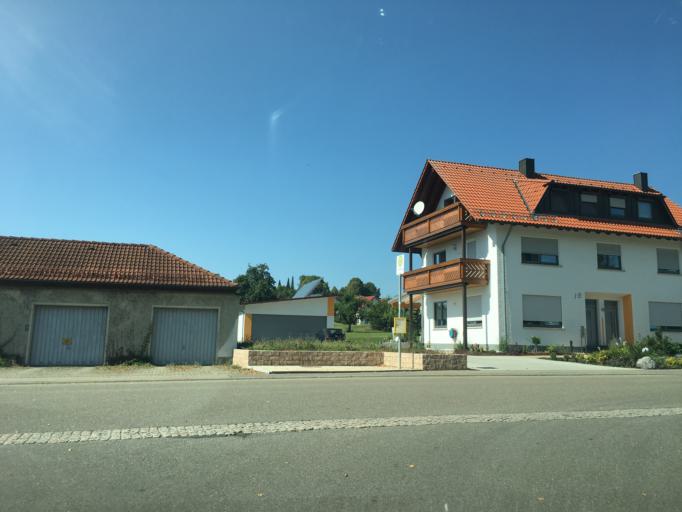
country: DE
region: Baden-Wuerttemberg
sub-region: Tuebingen Region
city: Hayingen
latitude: 48.2779
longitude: 9.4787
